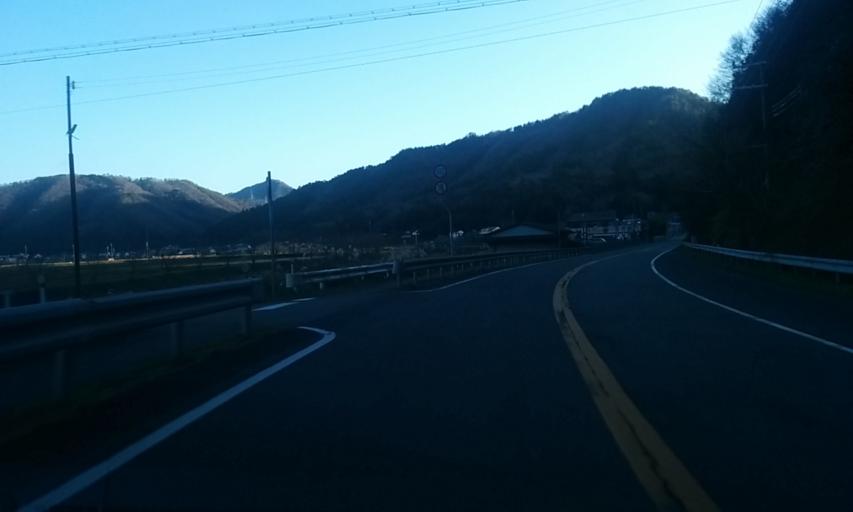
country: JP
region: Hyogo
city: Sasayama
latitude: 35.0778
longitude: 135.3313
